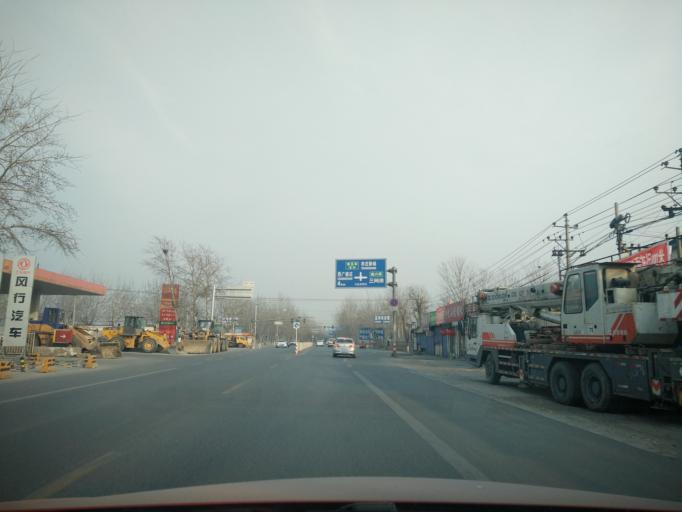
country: CN
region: Beijing
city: Yinghai
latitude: 39.7651
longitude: 116.4044
